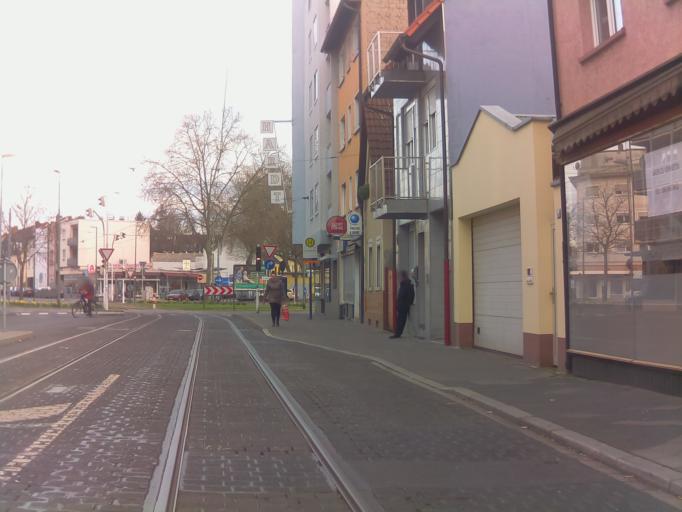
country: DE
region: Rheinland-Pfalz
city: Ludwigshafen am Rhein
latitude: 49.4978
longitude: 8.4194
